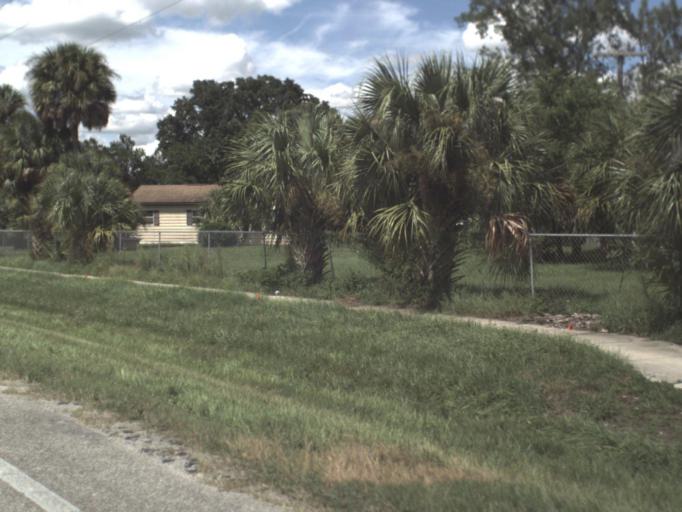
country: US
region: Florida
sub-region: Polk County
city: Willow Oak
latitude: 27.9165
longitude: -82.0225
